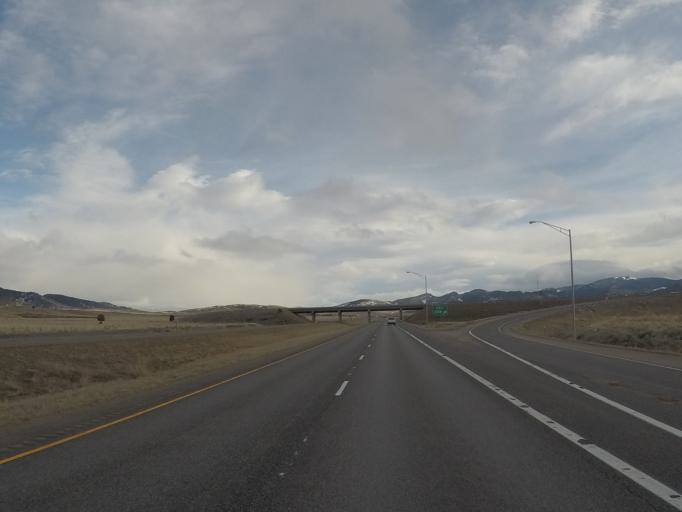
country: US
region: Montana
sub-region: Deer Lodge County
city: Warm Springs
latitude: 46.0979
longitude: -112.7936
